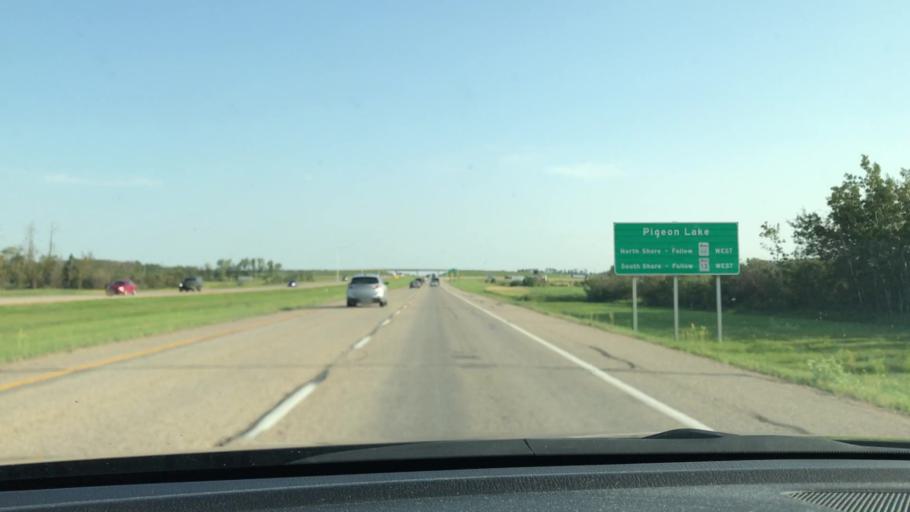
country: CA
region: Alberta
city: Millet
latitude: 53.0992
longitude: -113.5984
